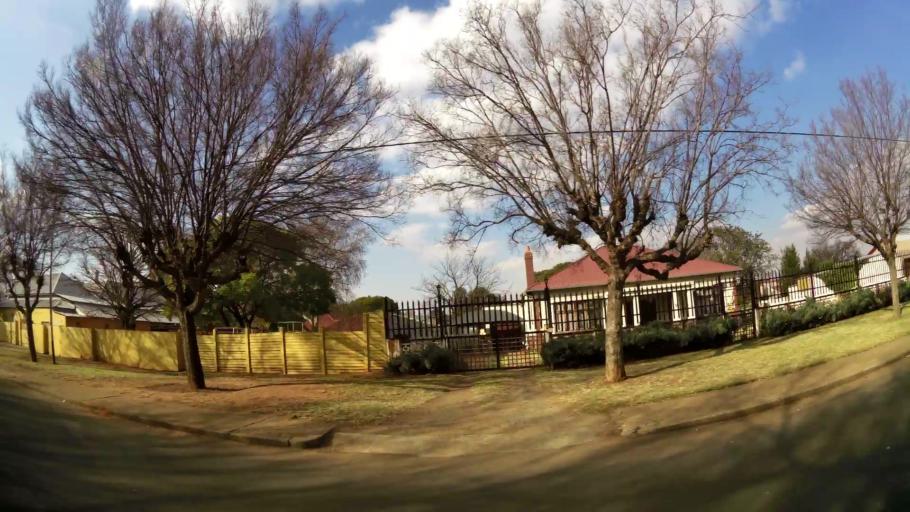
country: ZA
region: Gauteng
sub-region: West Rand District Municipality
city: Krugersdorp
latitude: -26.0849
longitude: 27.7726
